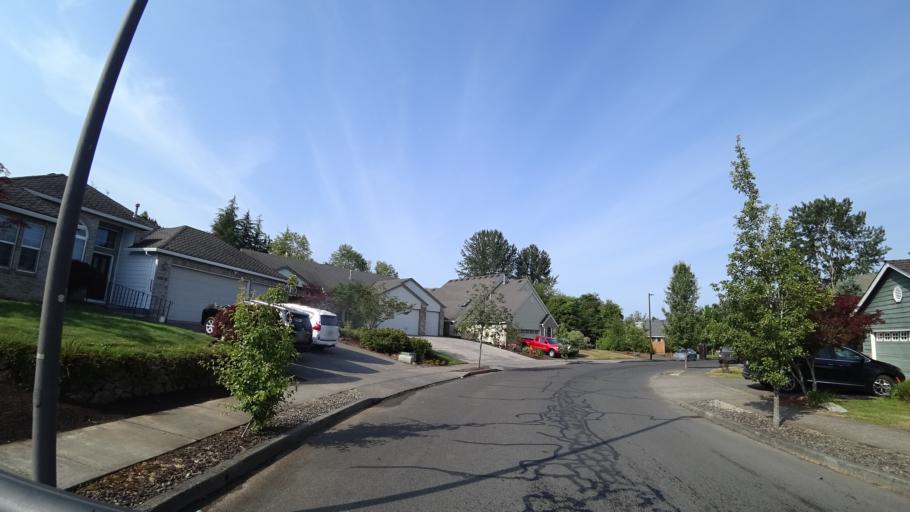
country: US
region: Oregon
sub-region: Clackamas County
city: Happy Valley
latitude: 45.4454
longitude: -122.5194
